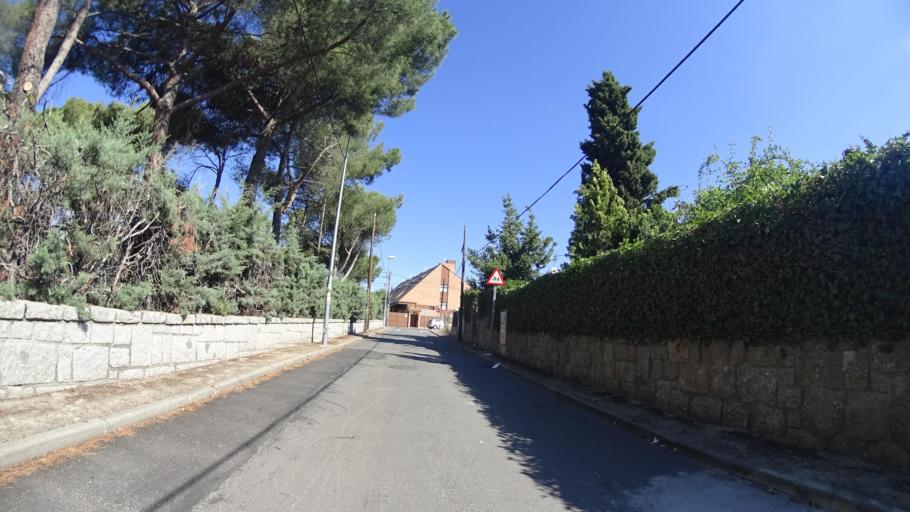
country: ES
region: Madrid
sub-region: Provincia de Madrid
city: Las Matas
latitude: 40.5490
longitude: -3.8921
